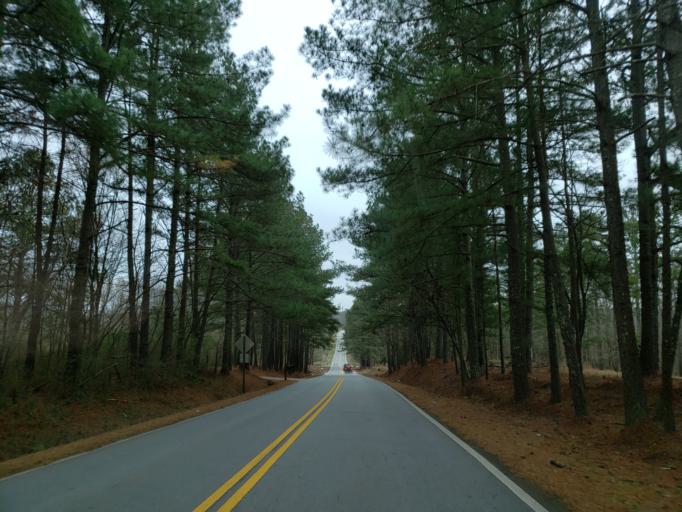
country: US
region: Georgia
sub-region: Paulding County
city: Hiram
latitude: 33.9154
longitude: -84.7239
